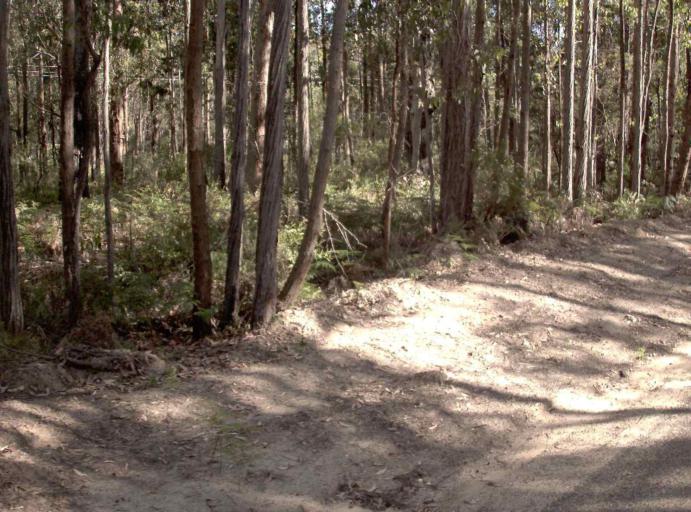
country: AU
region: Victoria
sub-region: East Gippsland
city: Lakes Entrance
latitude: -37.6854
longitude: 148.0501
